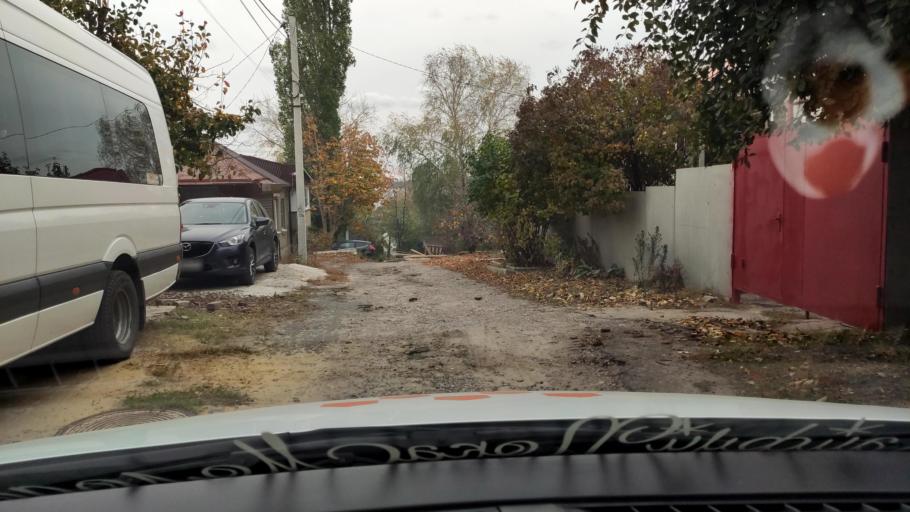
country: RU
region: Voronezj
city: Voronezh
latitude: 51.6328
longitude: 39.1974
